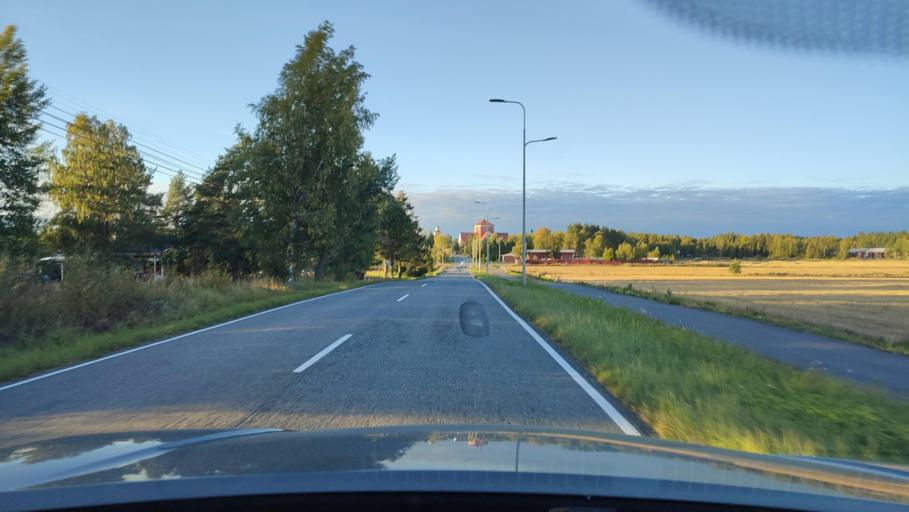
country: FI
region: Ostrobothnia
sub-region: Sydosterbotten
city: Kristinestad
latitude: 62.2408
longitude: 21.5209
